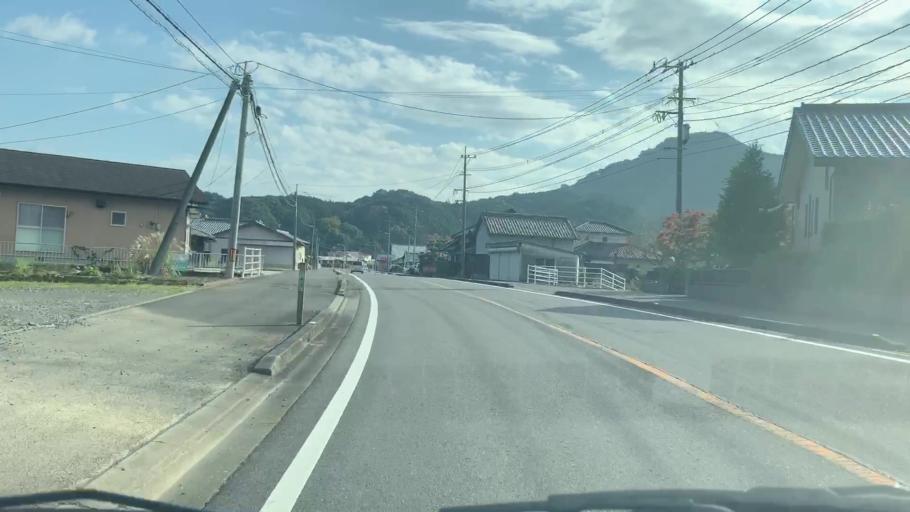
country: JP
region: Saga Prefecture
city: Takeocho-takeo
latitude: 33.1711
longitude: 130.0497
